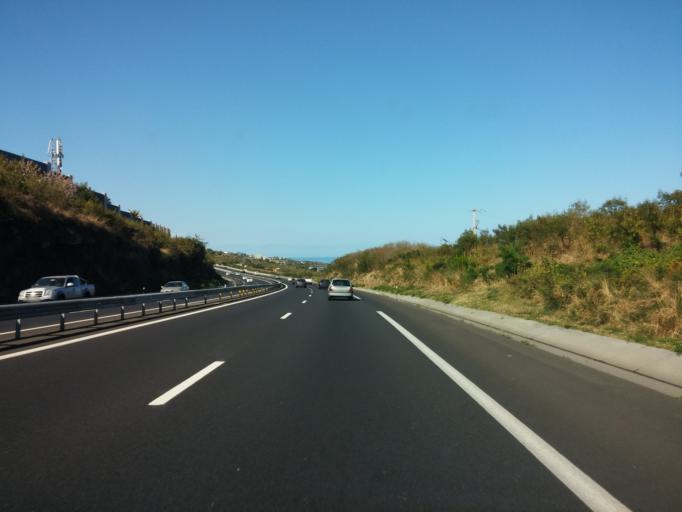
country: RE
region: Reunion
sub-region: Reunion
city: Saint-Leu
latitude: -21.1792
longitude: 55.2965
